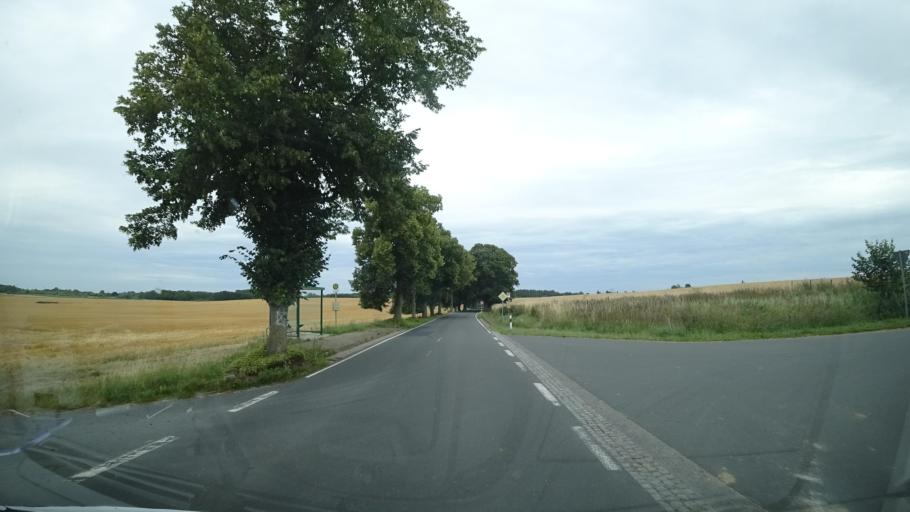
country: DE
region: Mecklenburg-Vorpommern
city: Poseritz
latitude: 54.3032
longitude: 13.2413
